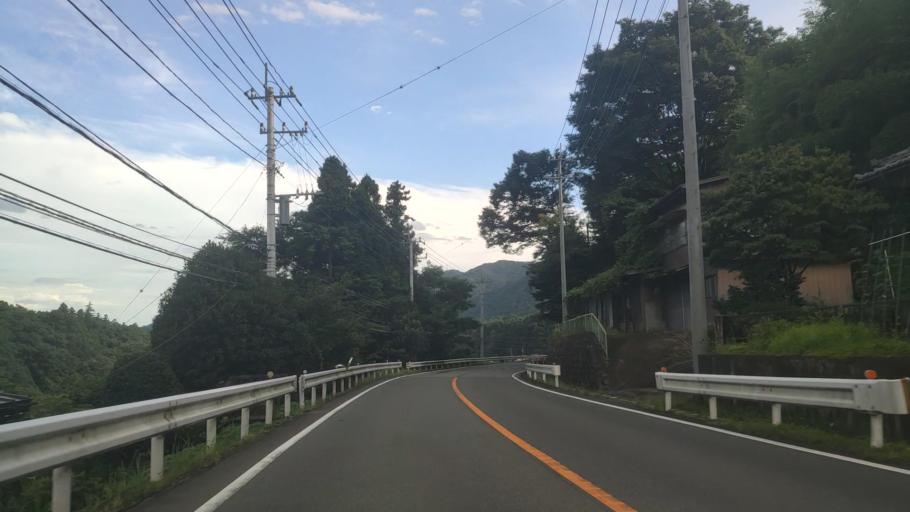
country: JP
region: Gunma
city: Omamacho-omama
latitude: 36.4730
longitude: 139.2579
